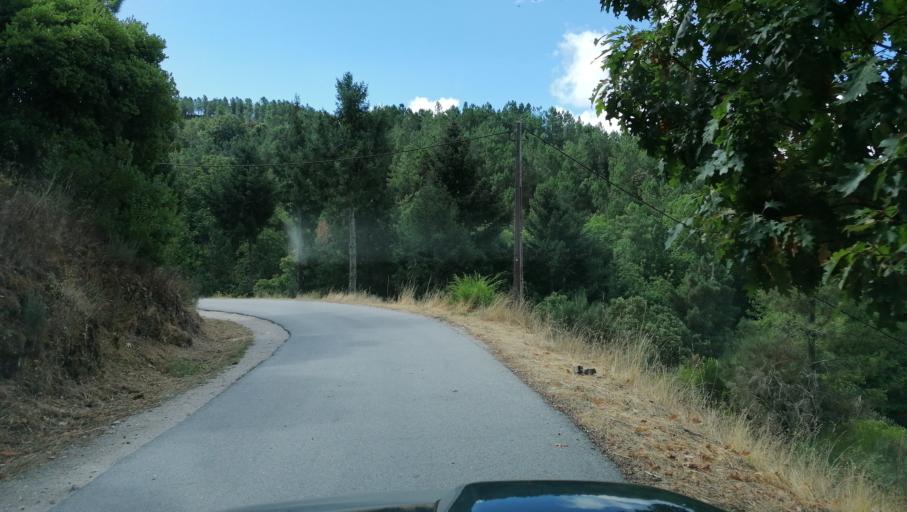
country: PT
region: Vila Real
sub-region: Vila Pouca de Aguiar
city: Vila Pouca de Aguiar
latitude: 41.5345
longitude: -7.5961
